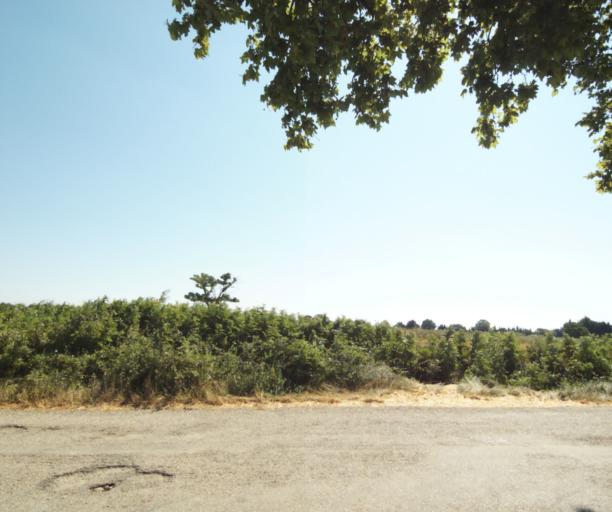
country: FR
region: Languedoc-Roussillon
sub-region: Departement de l'Herault
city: Marsillargues
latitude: 43.6559
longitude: 4.1652
